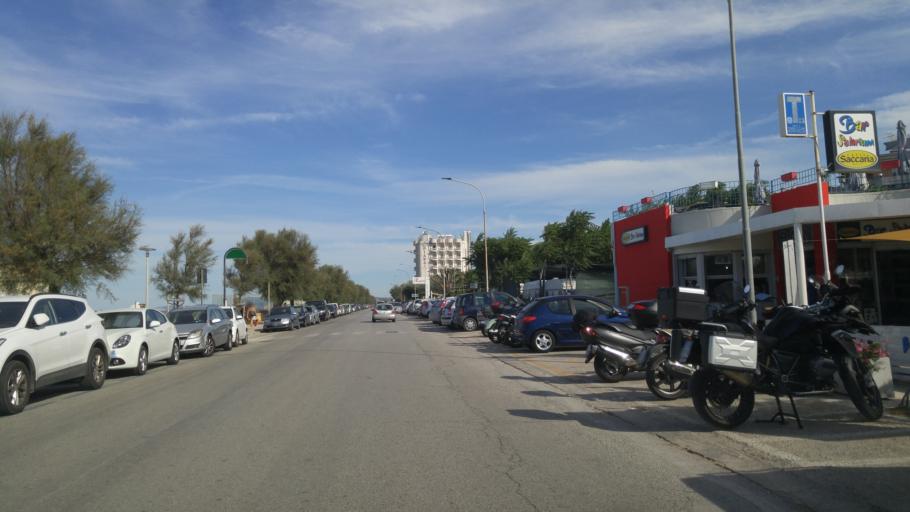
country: IT
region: The Marches
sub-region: Provincia di Ancona
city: Montignano-Marzocca
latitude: 43.6954
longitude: 13.2563
